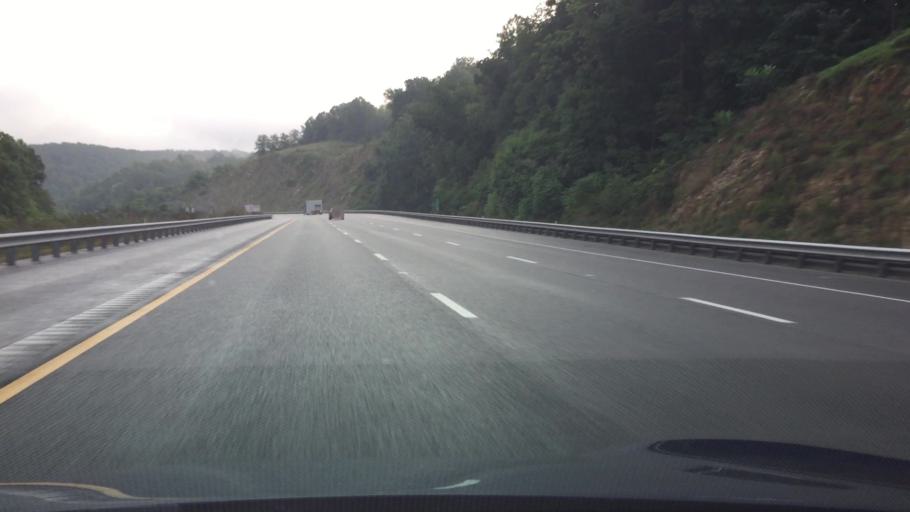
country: US
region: Virginia
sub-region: Montgomery County
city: Shawsville
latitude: 37.1684
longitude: -80.3152
